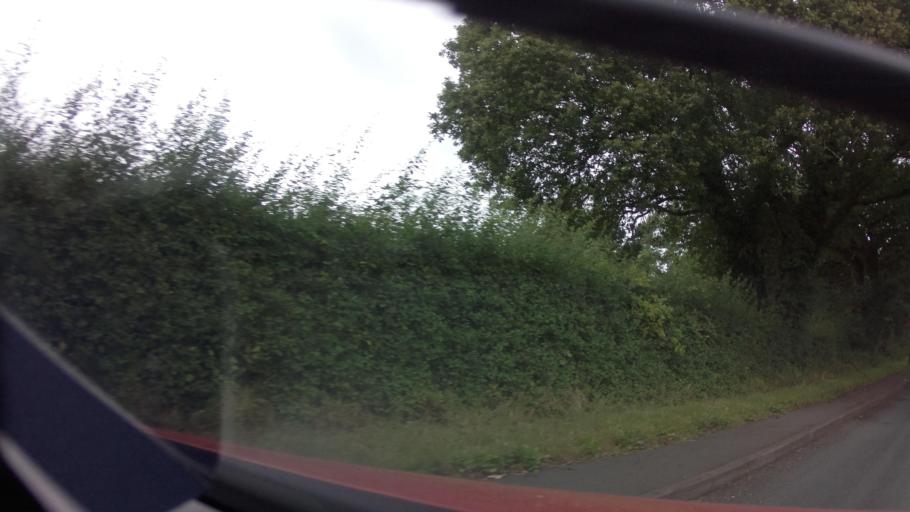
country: GB
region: England
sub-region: Solihull
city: Cheswick Green
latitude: 52.3837
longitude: -1.8221
